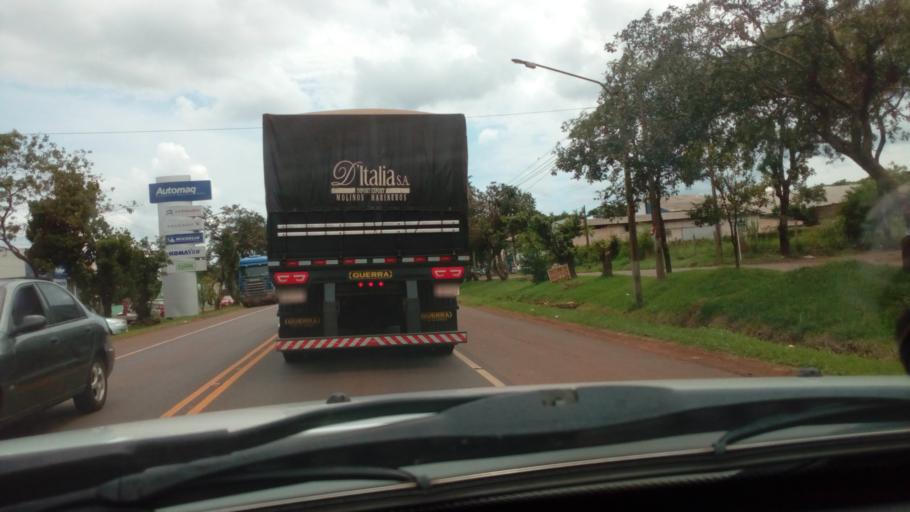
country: PY
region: Alto Parana
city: Santa Rita
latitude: -25.7850
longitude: -55.0806
